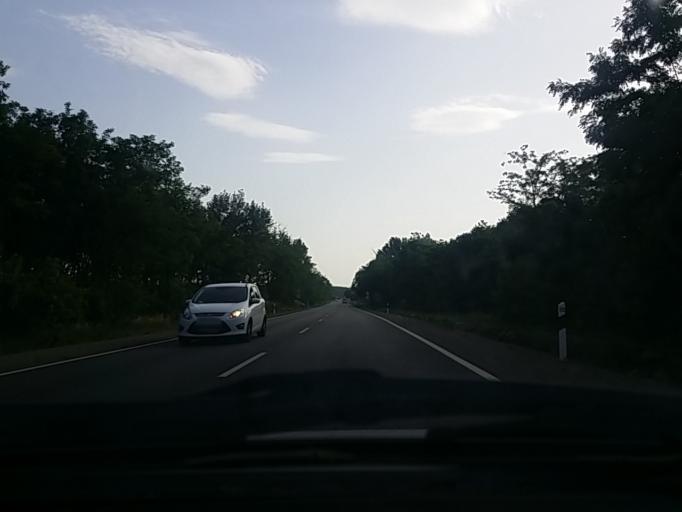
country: HU
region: Jasz-Nagykun-Szolnok
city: Jaszbereny
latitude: 47.4626
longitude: 19.8466
